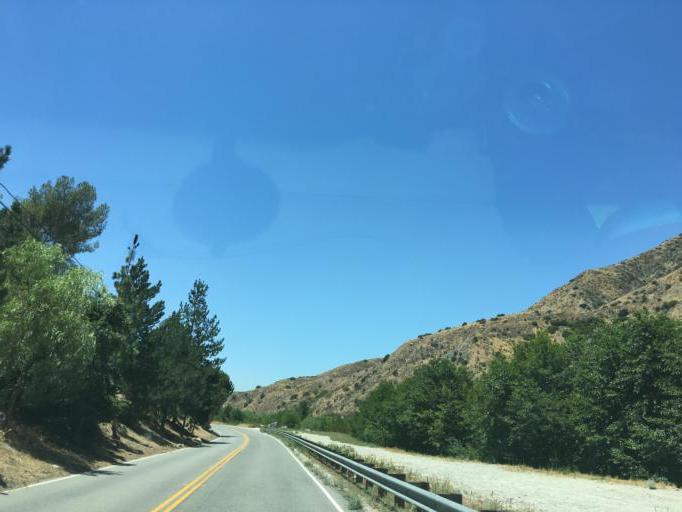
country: US
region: California
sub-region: Los Angeles County
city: La Crescenta-Montrose
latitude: 34.2903
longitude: -118.2892
